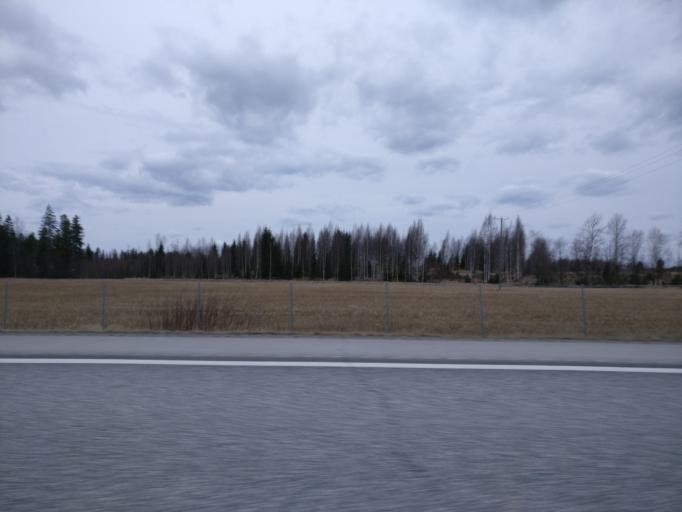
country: FI
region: Uusimaa
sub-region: Helsinki
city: Hyvinge
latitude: 60.6023
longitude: 24.7995
